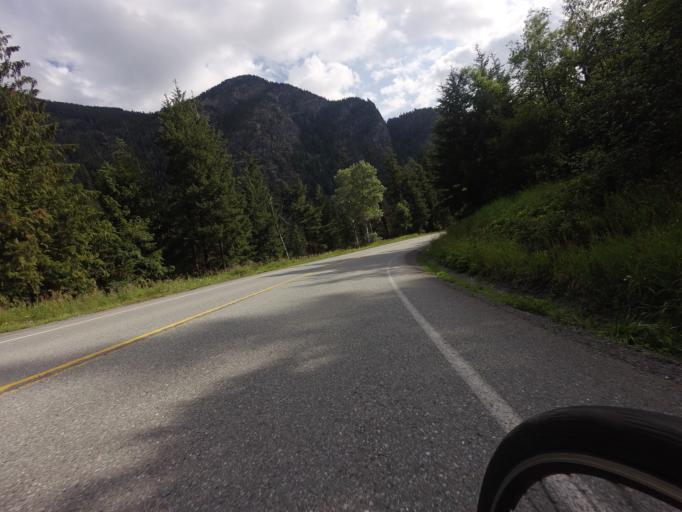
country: CA
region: British Columbia
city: Lillooet
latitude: 50.6383
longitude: -122.0884
